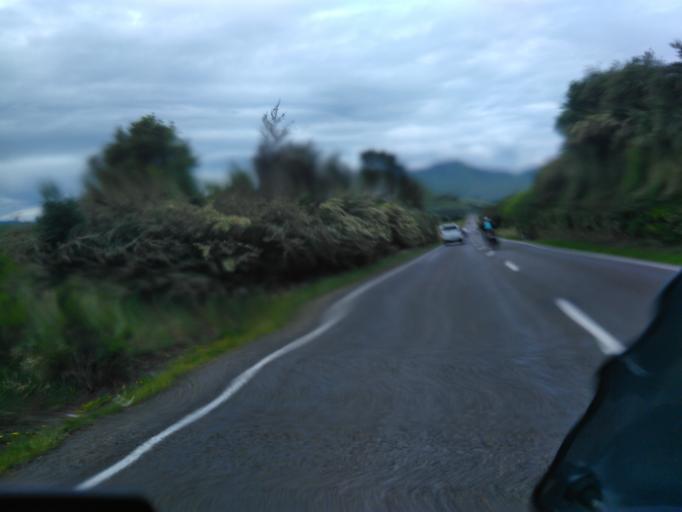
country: NZ
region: Bay of Plenty
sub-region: Opotiki District
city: Opotiki
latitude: -38.3631
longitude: 177.4930
